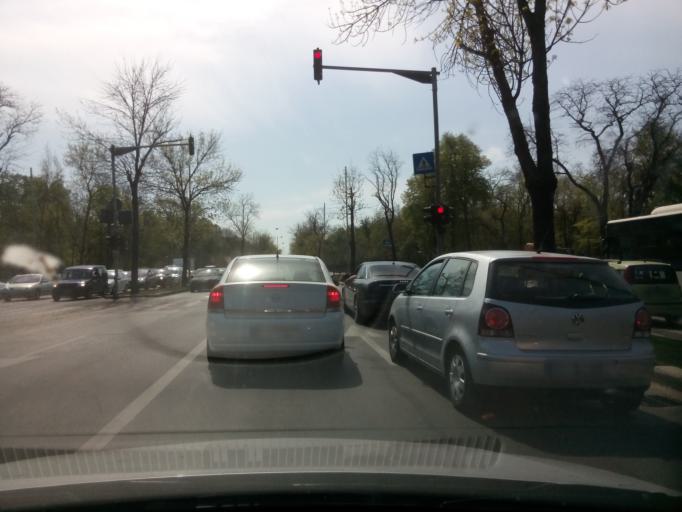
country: RO
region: Bucuresti
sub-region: Municipiul Bucuresti
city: Bucuresti
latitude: 44.4759
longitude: 26.0737
